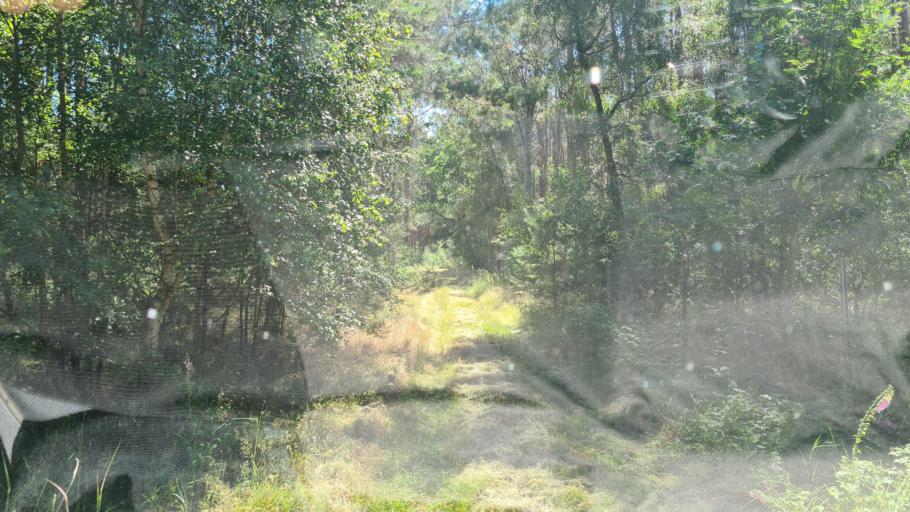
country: DE
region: Brandenburg
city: Treuenbrietzen
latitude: 52.0291
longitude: 12.8579
